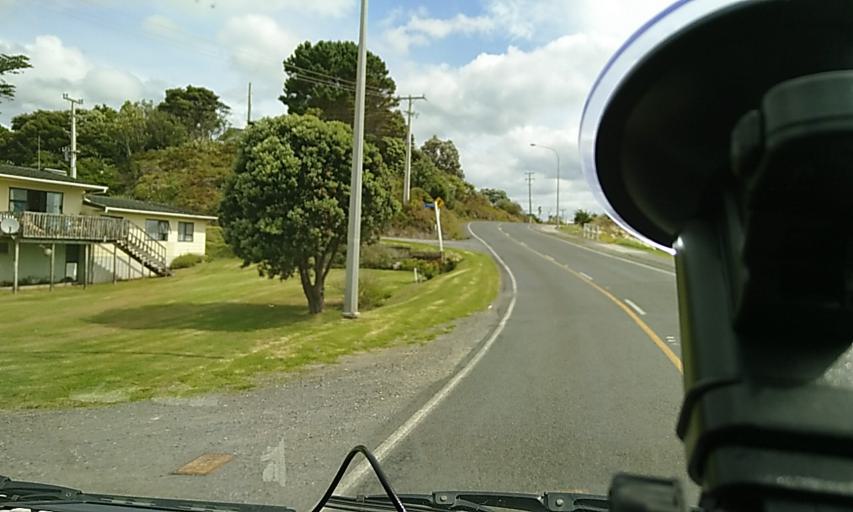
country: NZ
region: Northland
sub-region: Far North District
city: Ahipara
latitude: -35.5171
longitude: 173.3885
